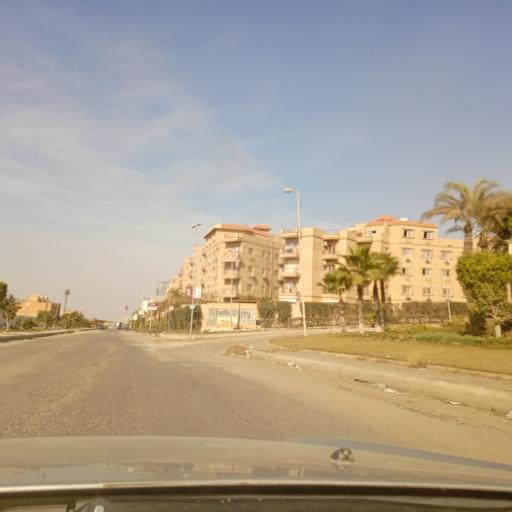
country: EG
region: Muhafazat al Qalyubiyah
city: Al Khankah
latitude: 30.0325
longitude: 31.4852
